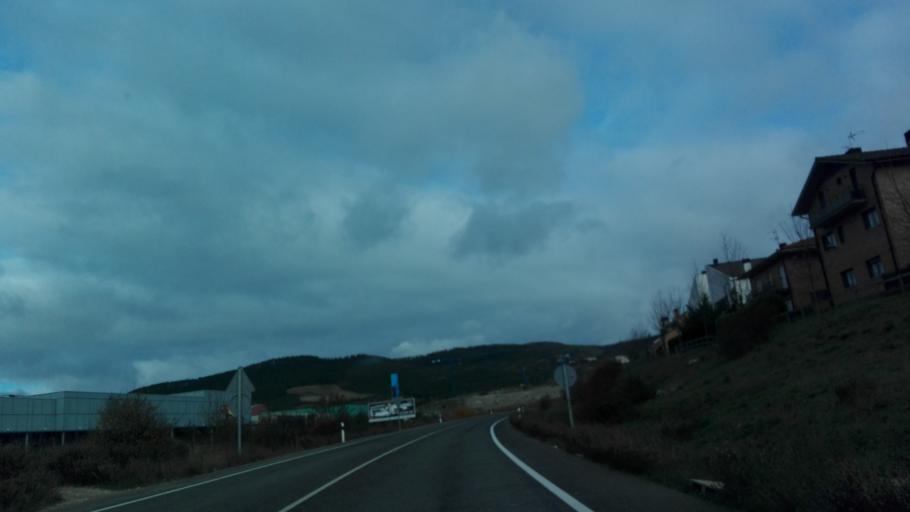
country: ES
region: Navarre
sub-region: Provincia de Navarra
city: Egues-Uharte
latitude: 42.8268
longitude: -1.5837
